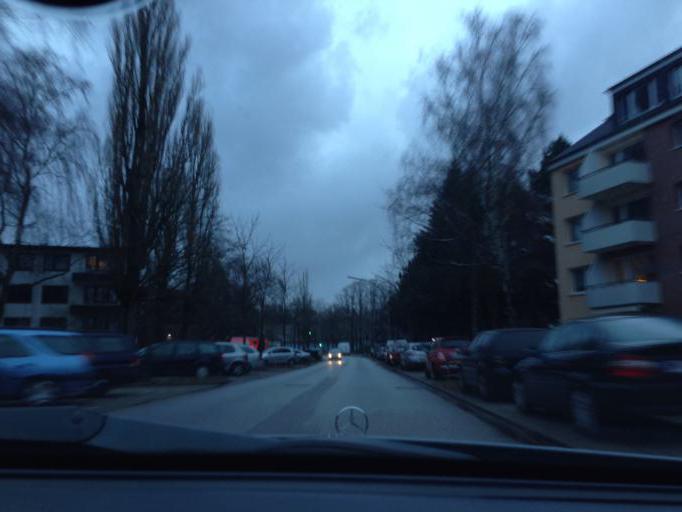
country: DE
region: Hamburg
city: Farmsen-Berne
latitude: 53.6023
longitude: 10.1191
